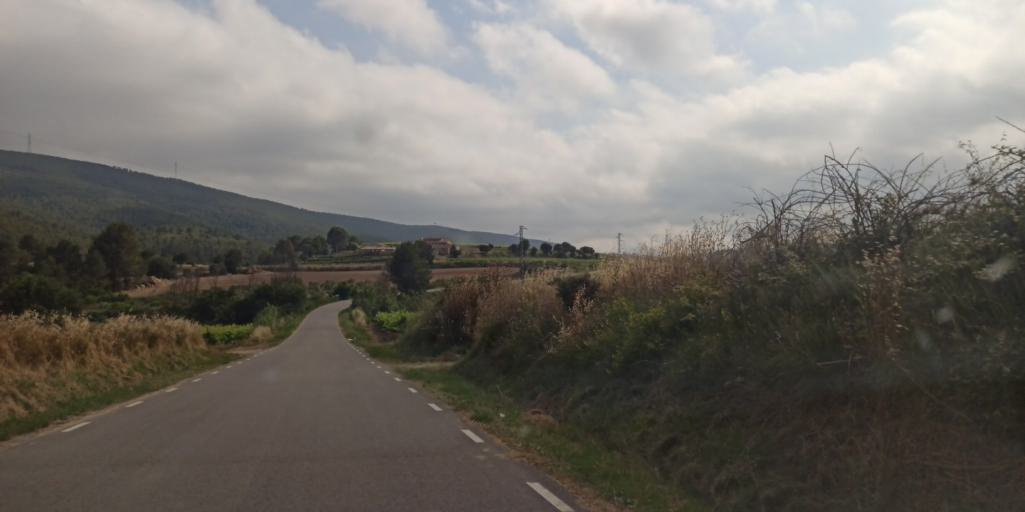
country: ES
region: Catalonia
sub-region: Provincia de Barcelona
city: Sant Joan de Mediona
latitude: 41.4687
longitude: 1.5960
